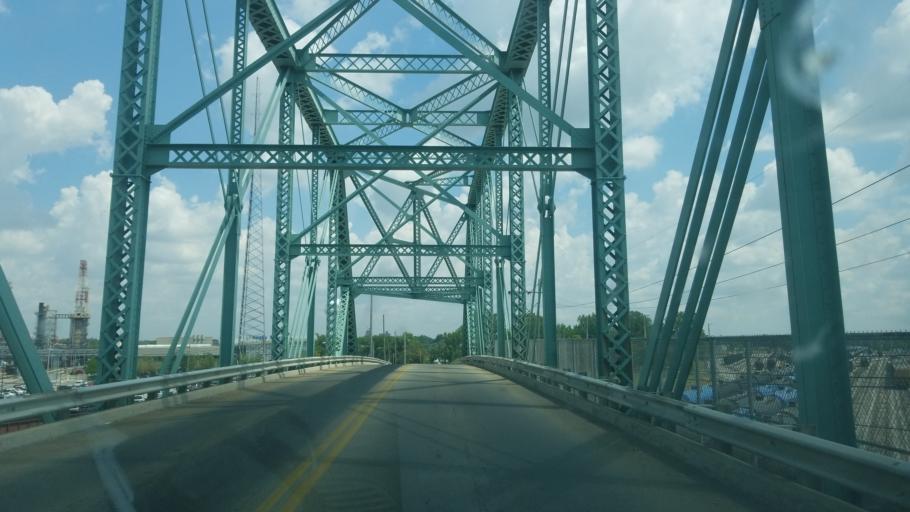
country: US
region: Ohio
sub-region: Allen County
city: Lima
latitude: 40.7177
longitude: -84.1143
